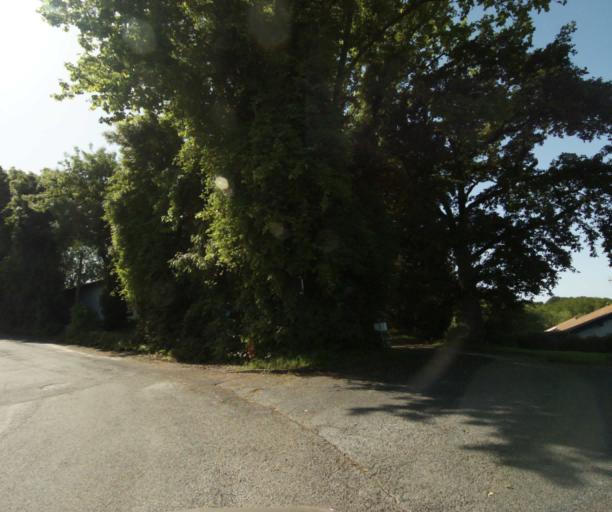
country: FR
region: Aquitaine
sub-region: Departement des Pyrenees-Atlantiques
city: Villefranque
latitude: 43.4575
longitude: -1.4494
